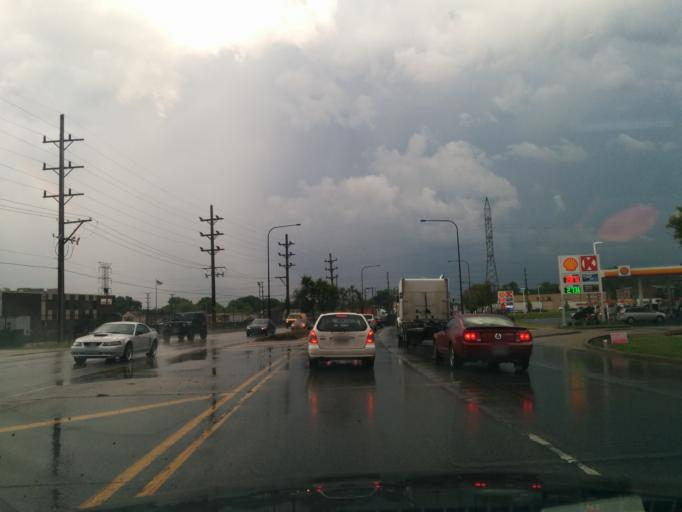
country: US
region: Illinois
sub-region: Cook County
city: Bridgeview
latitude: 41.7649
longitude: -87.8006
